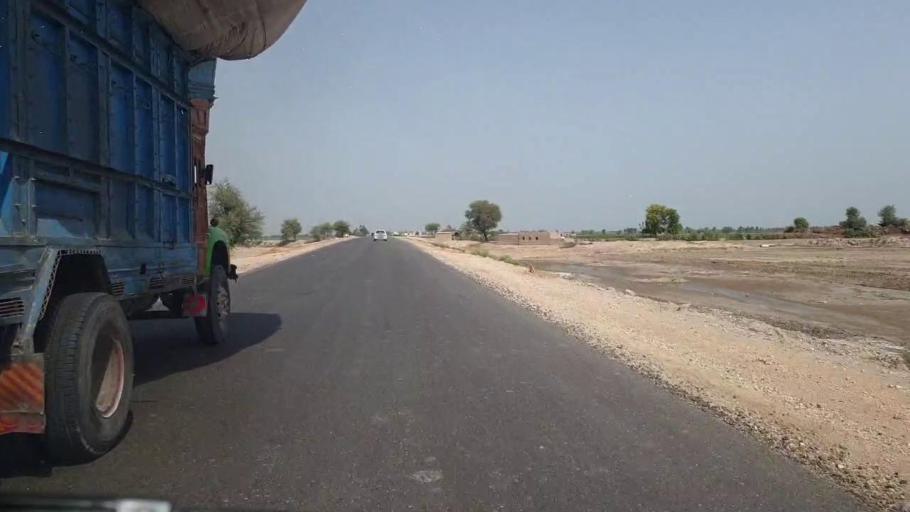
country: PK
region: Sindh
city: Sakrand
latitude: 26.2670
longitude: 68.1703
